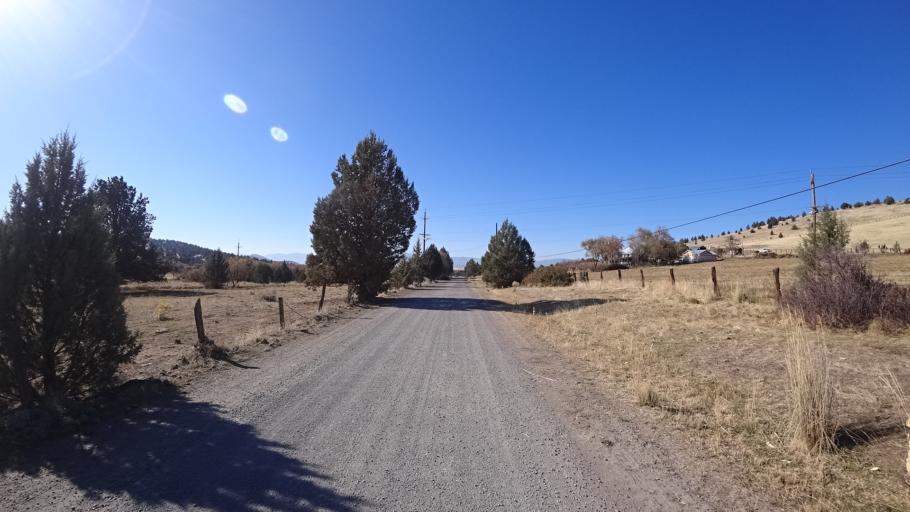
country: US
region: California
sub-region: Siskiyou County
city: Montague
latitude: 41.7292
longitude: -122.3617
